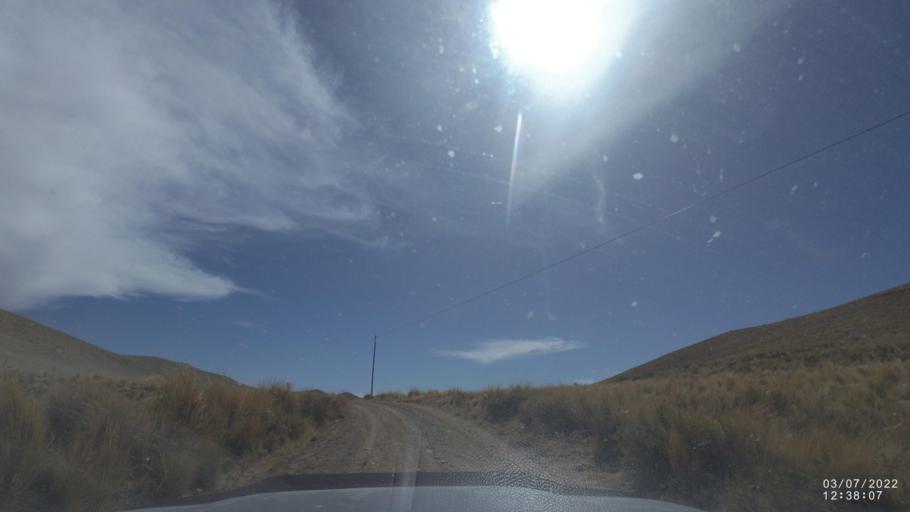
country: BO
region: Cochabamba
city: Irpa Irpa
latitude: -17.7940
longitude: -66.6174
